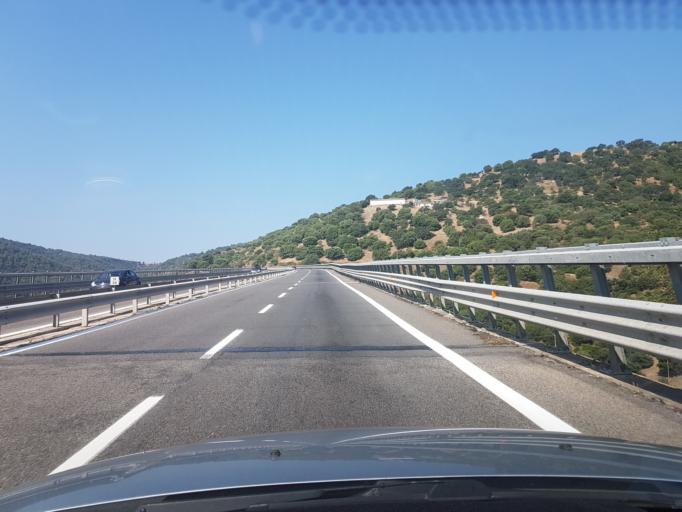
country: IT
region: Sardinia
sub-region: Provincia di Nuoro
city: Nuoro
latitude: 40.3440
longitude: 9.3181
